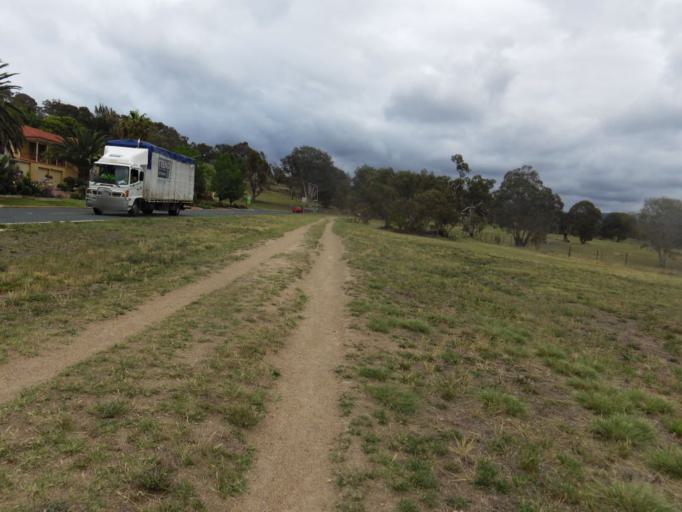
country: AU
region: Australian Capital Territory
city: Macquarie
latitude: -35.3492
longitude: 149.0250
